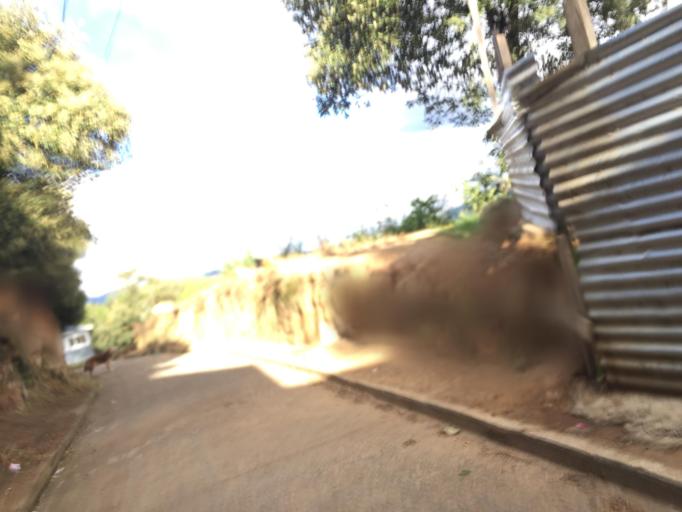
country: GT
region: Totonicapan
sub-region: Municipio de Totonicapan
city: Totonicapan
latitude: 14.9091
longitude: -91.3657
